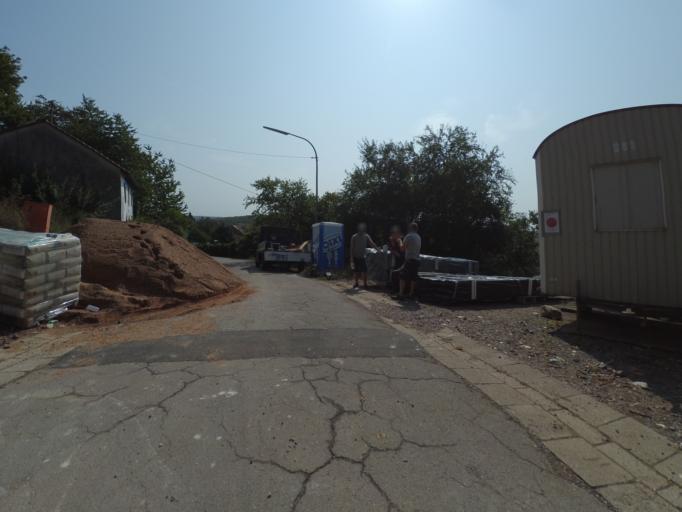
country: DE
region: Saarland
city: Orscholz
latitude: 49.4786
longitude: 6.5036
